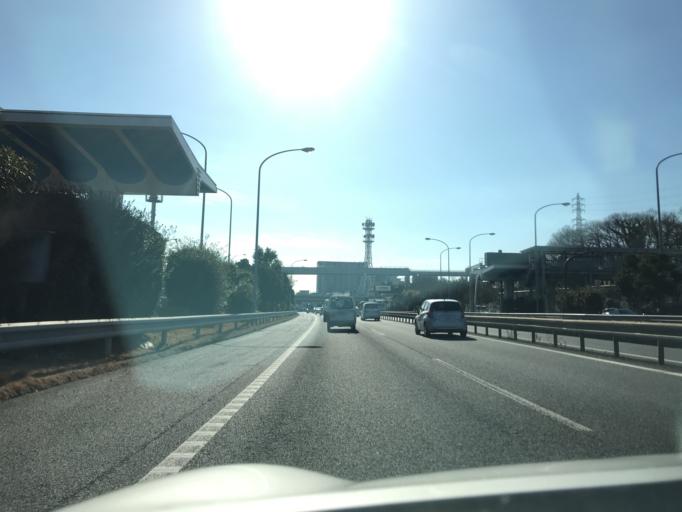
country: JP
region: Chiba
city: Chiba
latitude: 35.6437
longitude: 140.1121
